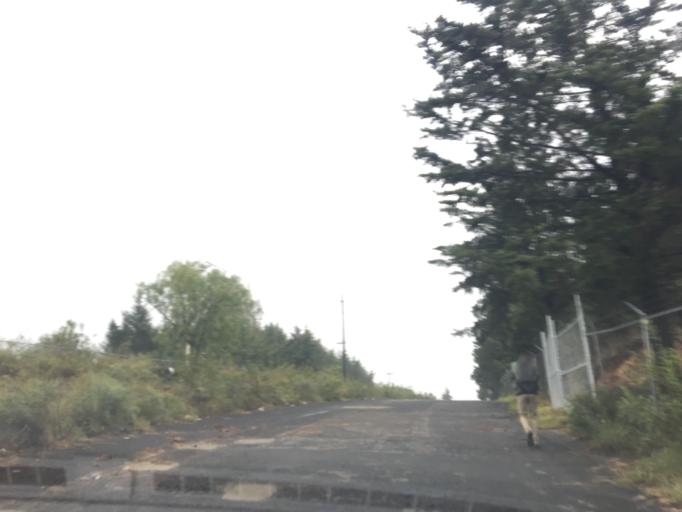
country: MX
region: Mexico
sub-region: Nicolas Romero
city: San Miguel Hila
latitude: 19.5707
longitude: -99.2991
